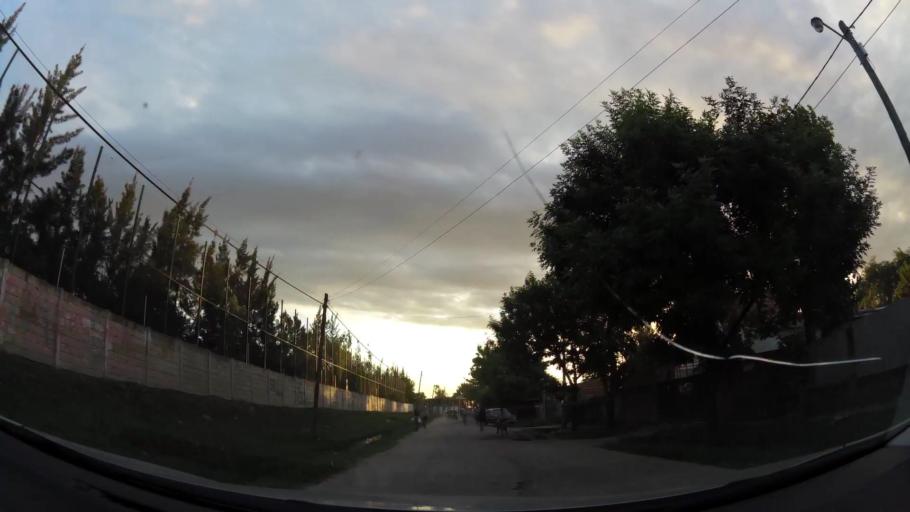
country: AR
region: Buenos Aires
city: Santa Catalina - Dique Lujan
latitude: -34.4368
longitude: -58.6657
